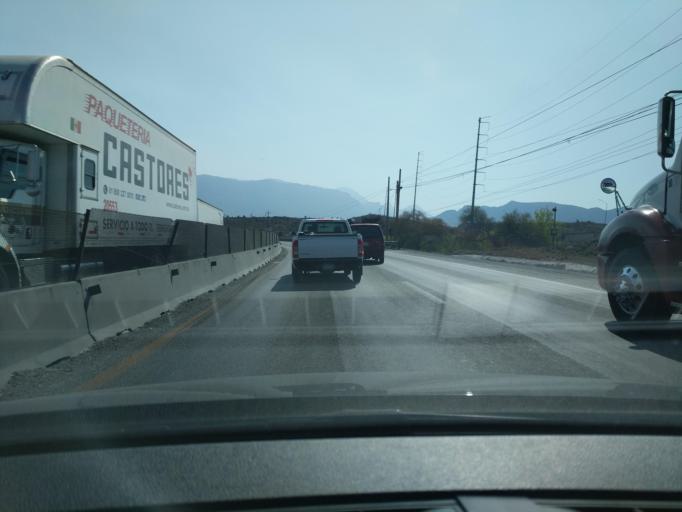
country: MX
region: Nuevo Leon
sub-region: Garcia
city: Los Parques
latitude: 25.7503
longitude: -100.5095
